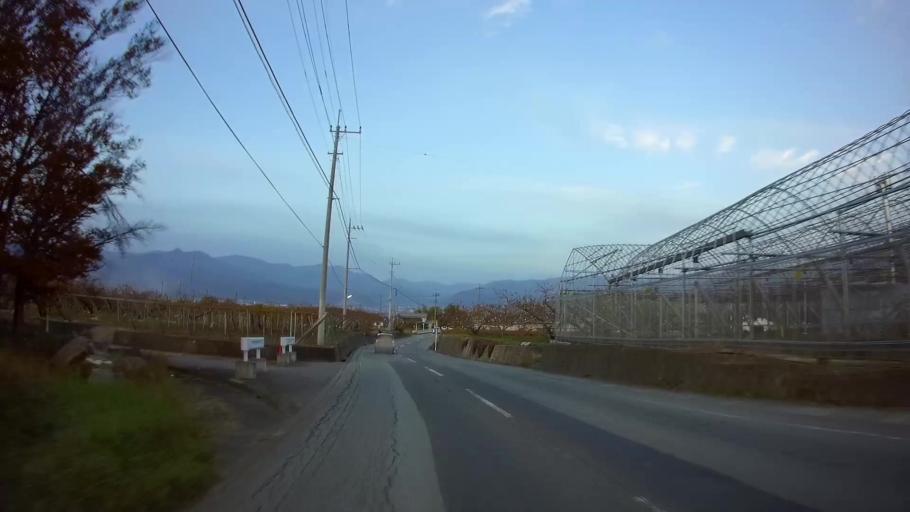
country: JP
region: Yamanashi
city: Isawa
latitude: 35.6514
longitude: 138.6888
